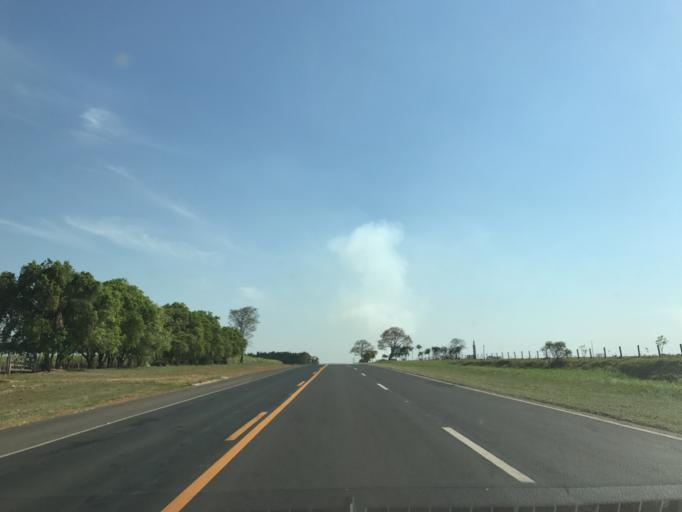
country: BR
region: Sao Paulo
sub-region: Penapolis
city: Penapolis
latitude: -21.3549
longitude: -50.0617
